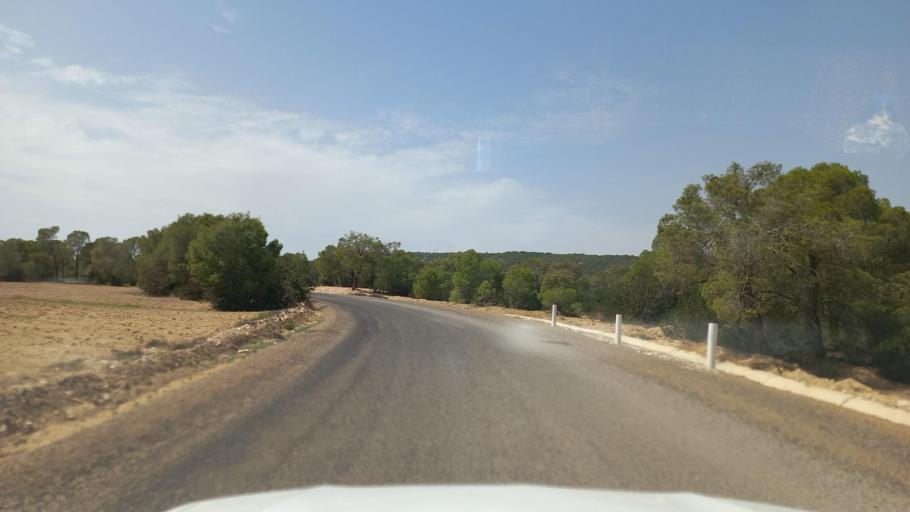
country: TN
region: Al Qasrayn
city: Sbiba
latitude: 35.3829
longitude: 8.9308
